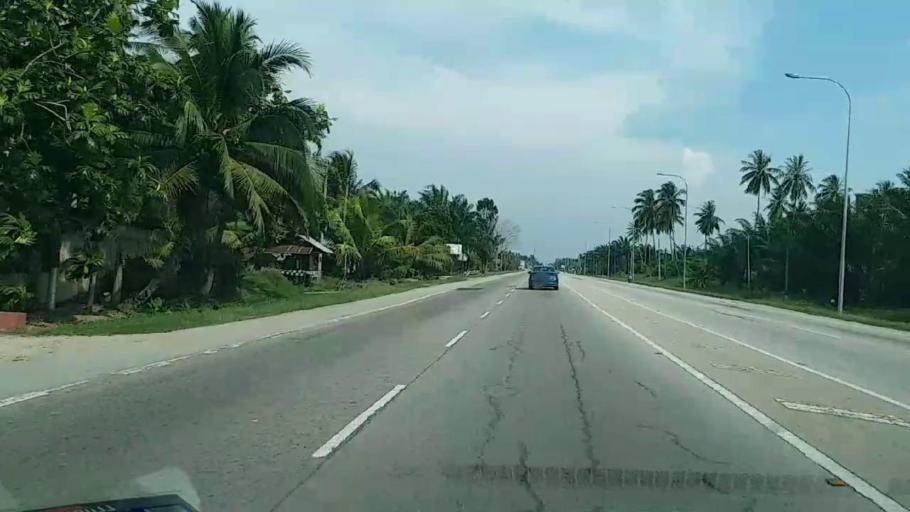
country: MY
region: Selangor
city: Kuala Selangor
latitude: 3.3759
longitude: 101.2371
